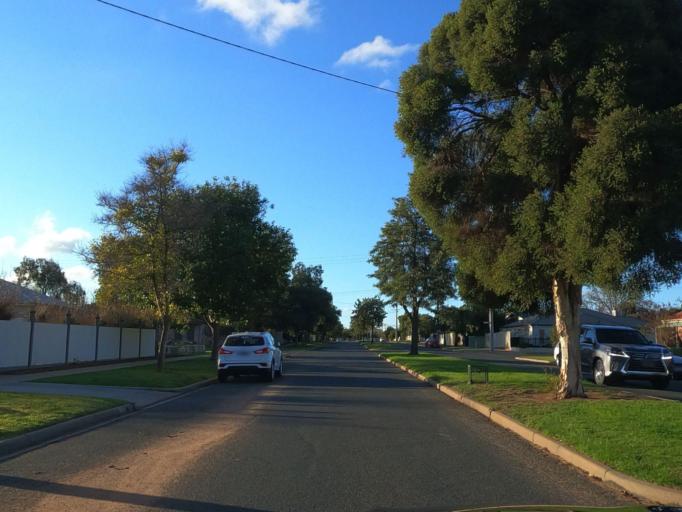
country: AU
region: Victoria
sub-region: Swan Hill
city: Swan Hill
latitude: -35.3471
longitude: 143.5555
